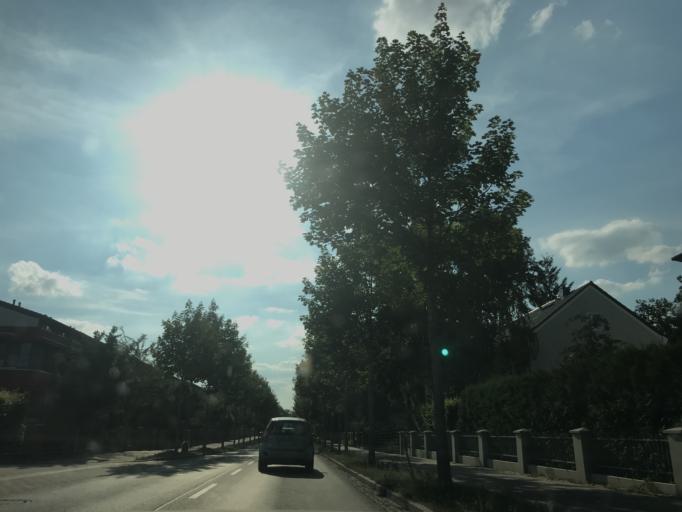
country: DE
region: Brandenburg
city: Kleinmachnow
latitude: 52.4050
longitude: 13.2245
